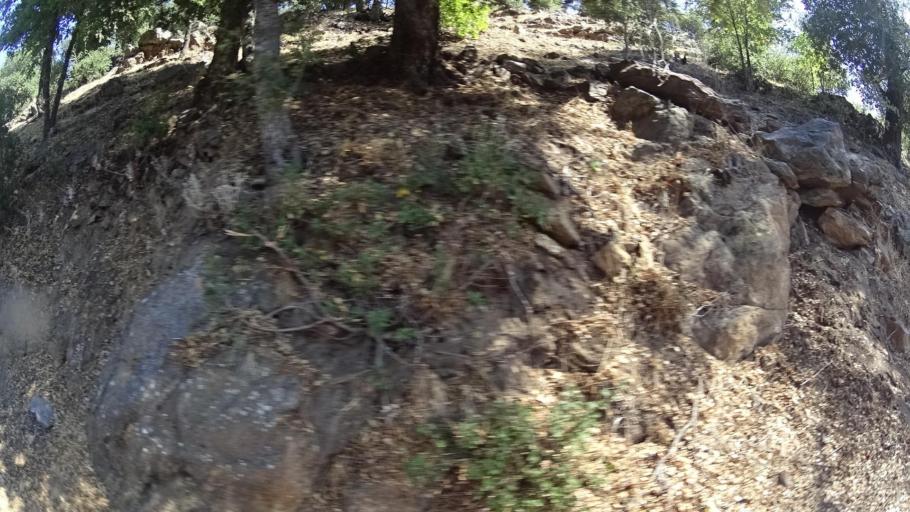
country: US
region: California
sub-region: San Diego County
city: Julian
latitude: 33.0677
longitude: -116.5898
